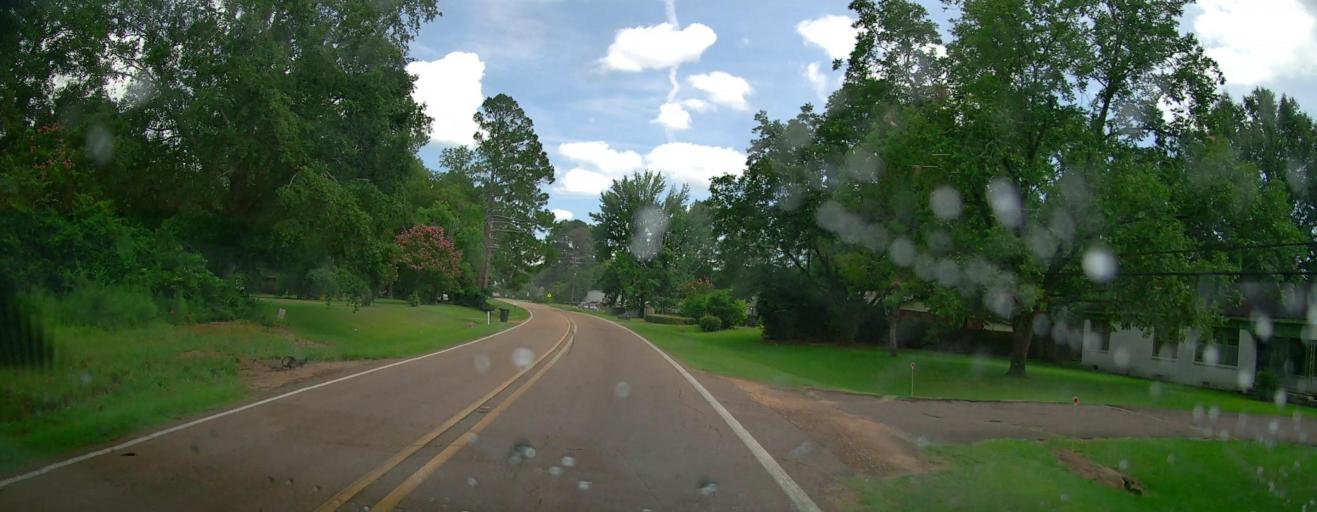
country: US
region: Mississippi
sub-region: Lee County
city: Shannon
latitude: 34.1236
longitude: -88.7173
